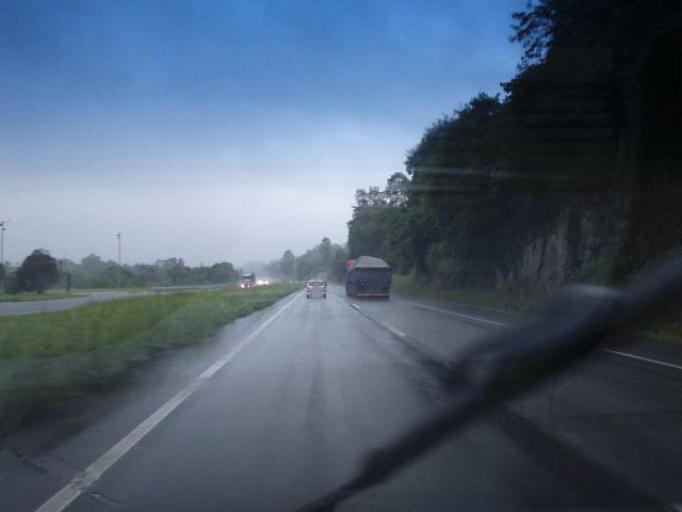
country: BR
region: Sao Paulo
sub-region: Miracatu
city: Miracatu
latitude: -24.2871
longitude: -47.4506
